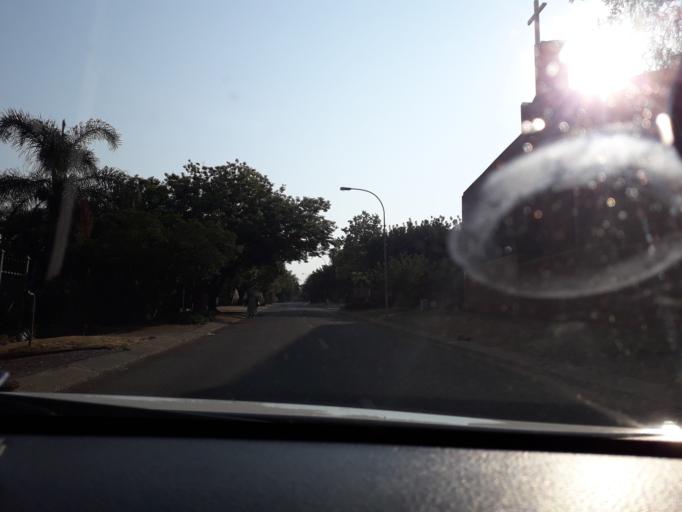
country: ZA
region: Gauteng
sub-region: City of Tshwane Metropolitan Municipality
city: Centurion
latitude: -25.8968
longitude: 28.1480
